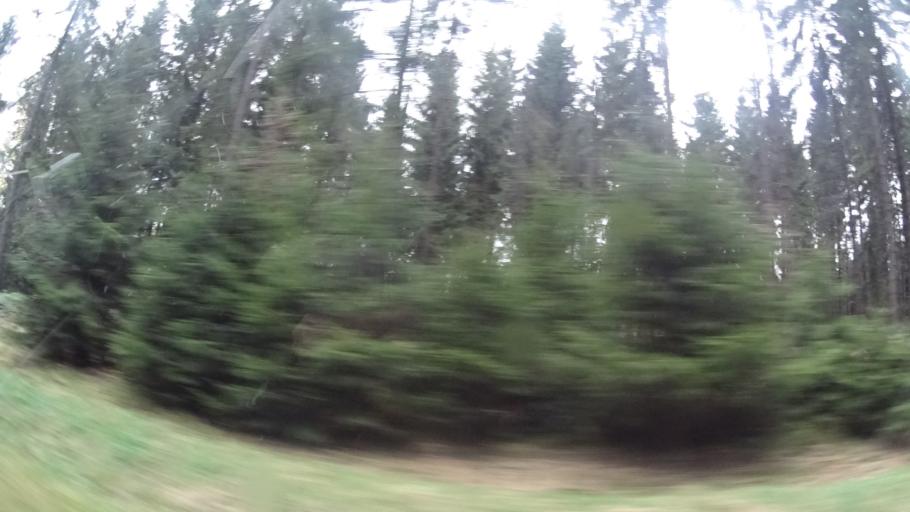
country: DE
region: Bavaria
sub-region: Upper Franconia
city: Tschirn
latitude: 50.4236
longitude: 11.4575
